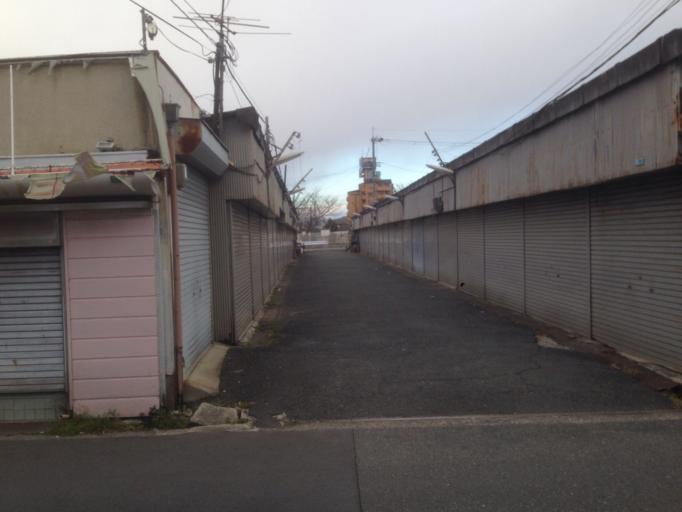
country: JP
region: Osaka
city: Matsubara
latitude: 34.6045
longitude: 135.5460
